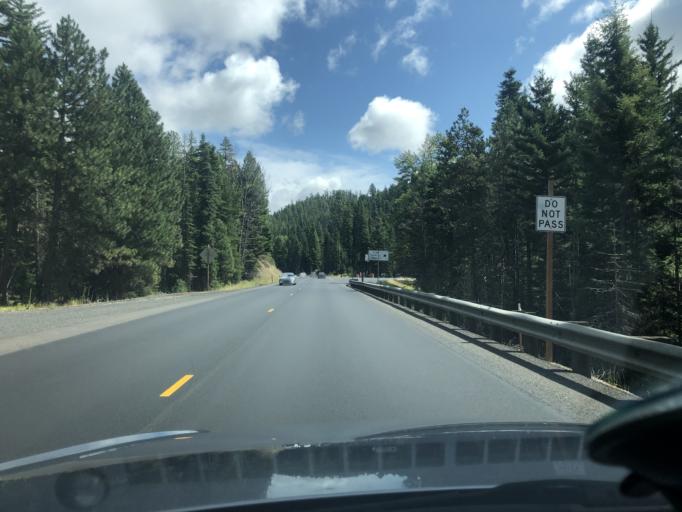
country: US
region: Washington
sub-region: Chelan County
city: Cashmere
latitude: 47.3301
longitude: -120.6489
